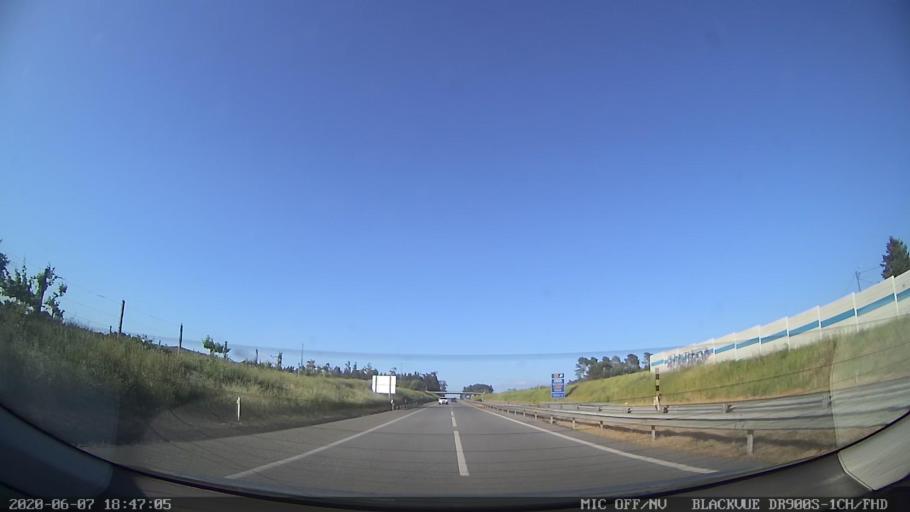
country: PT
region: Braga
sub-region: Vila Nova de Famalicao
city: Vila Nova de Famalicao
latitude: 41.3940
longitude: -8.4747
